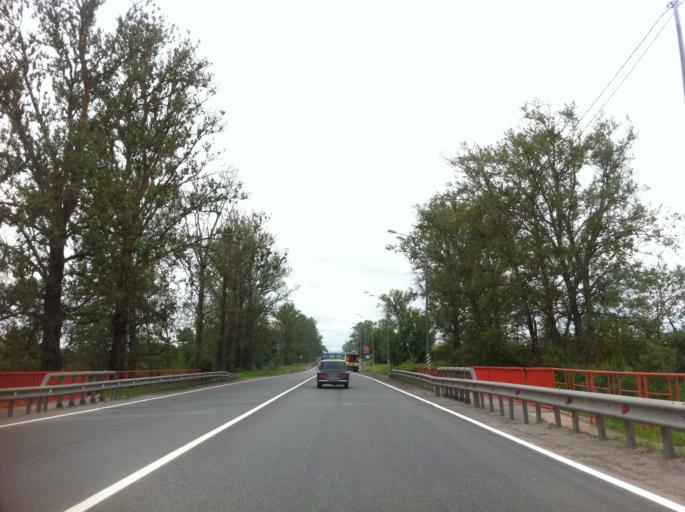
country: RU
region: Leningrad
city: Maloye Verevo
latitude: 59.6187
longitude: 30.1785
